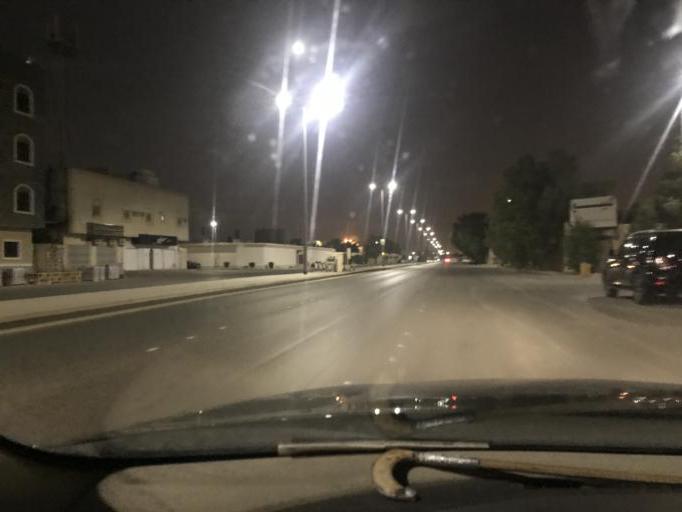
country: SA
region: Ar Riyad
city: Riyadh
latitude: 24.7279
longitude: 46.7916
